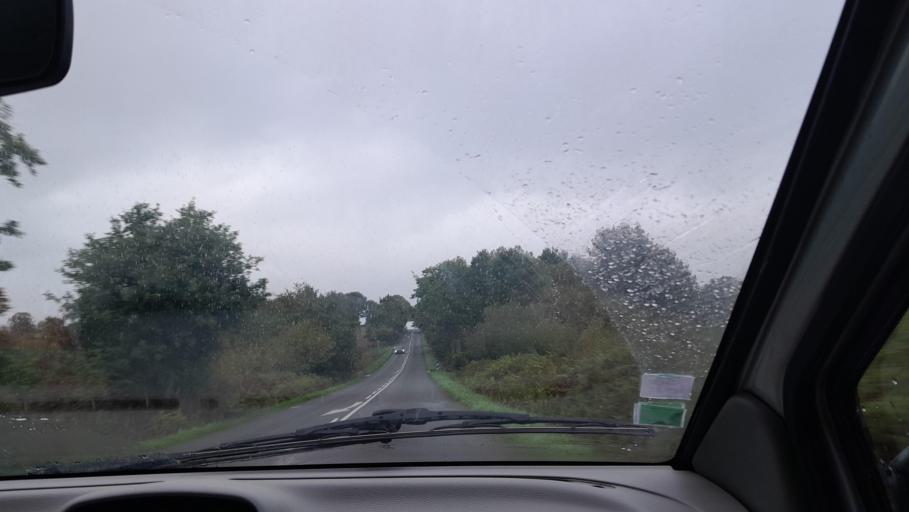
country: FR
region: Pays de la Loire
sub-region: Departement de la Mayenne
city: Congrier
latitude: 47.8638
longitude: -1.1318
